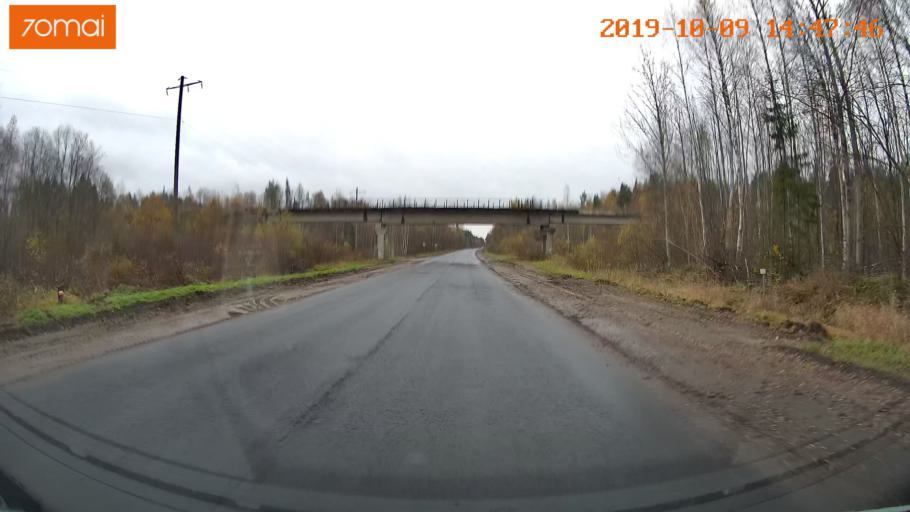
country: RU
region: Kostroma
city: Chistyye Bory
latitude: 58.4141
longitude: 41.5720
